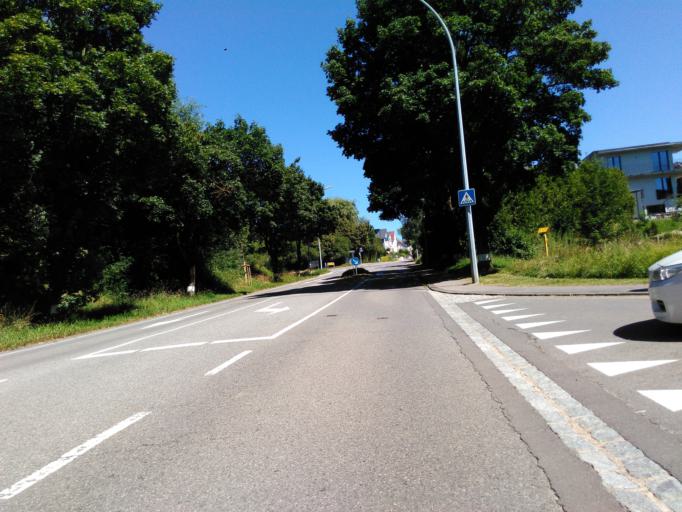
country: LU
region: Luxembourg
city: Bergem
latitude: 49.5101
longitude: 6.0492
